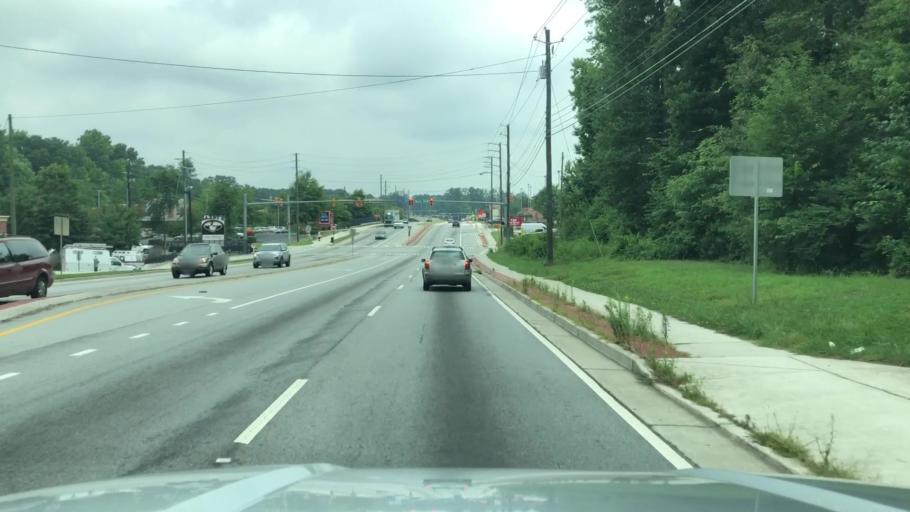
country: US
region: Georgia
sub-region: Cobb County
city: Mableton
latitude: 33.8300
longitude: -84.5758
